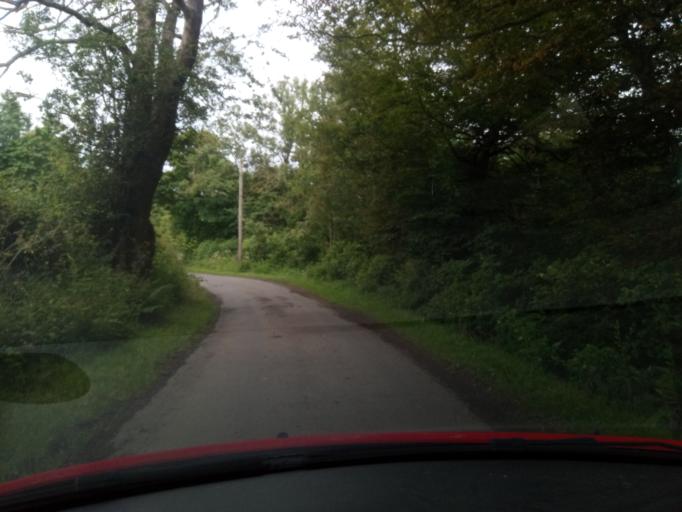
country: GB
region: Scotland
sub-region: The Scottish Borders
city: Hawick
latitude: 55.4570
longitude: -2.7321
